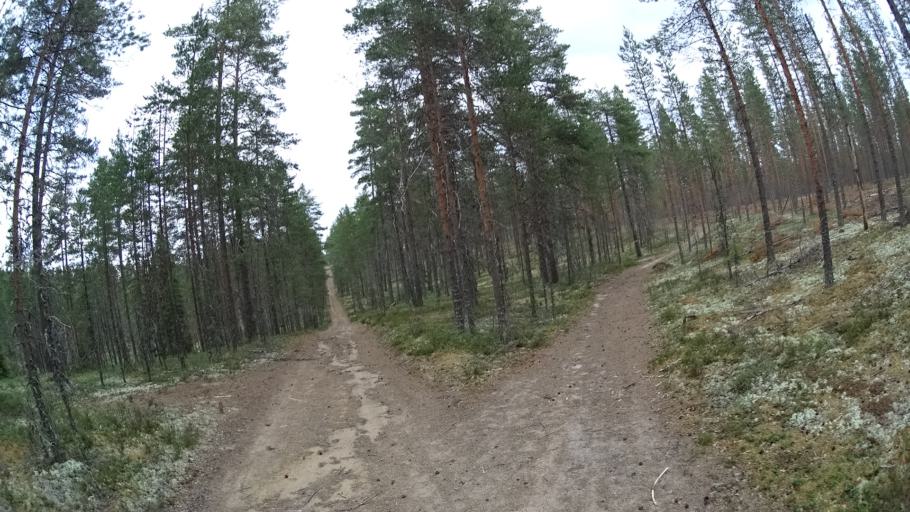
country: FI
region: Satakunta
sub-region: Pohjois-Satakunta
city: Jaemijaervi
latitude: 61.7677
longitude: 22.7897
